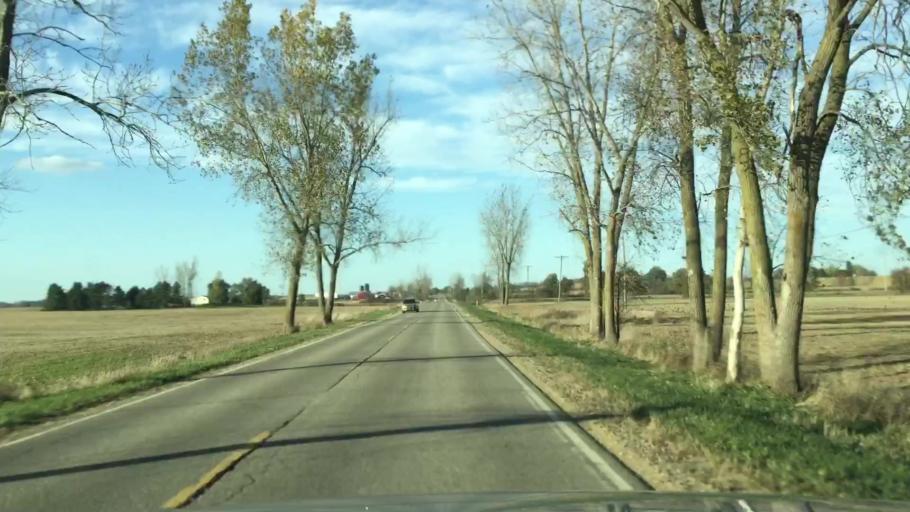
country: US
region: Michigan
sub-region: Lapeer County
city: North Branch
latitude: 43.3011
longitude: -83.1988
